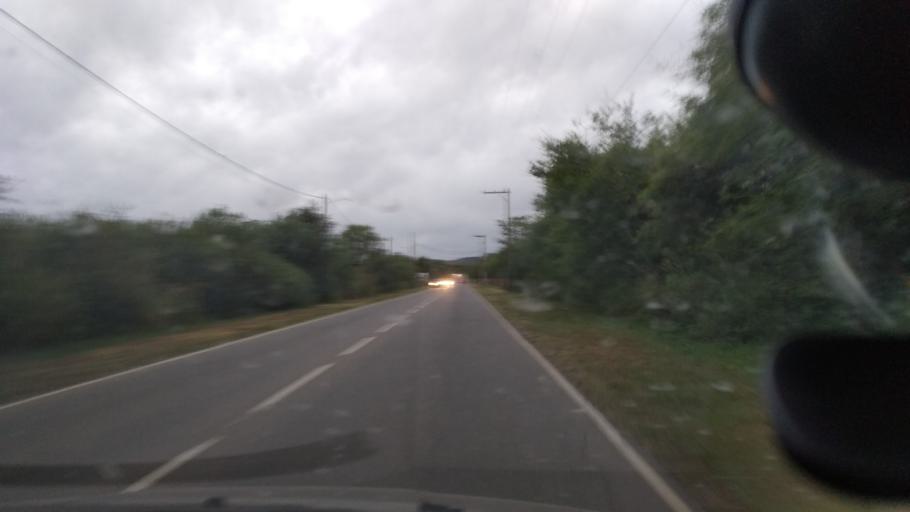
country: AR
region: Cordoba
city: Villa Las Rosas
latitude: -31.9329
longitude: -65.0392
